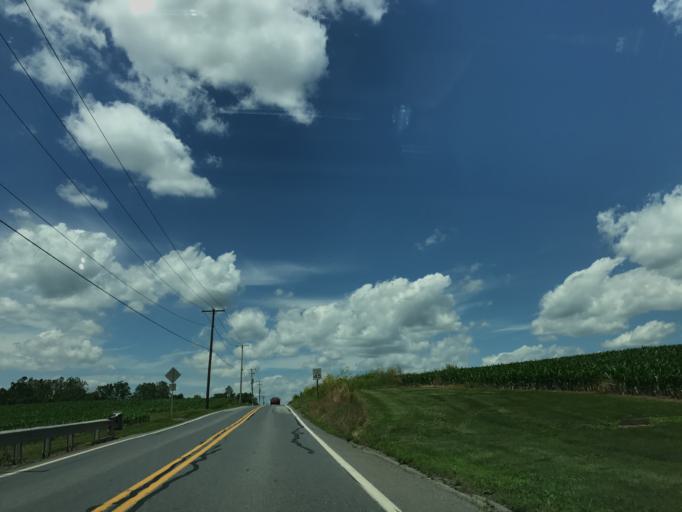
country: US
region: Pennsylvania
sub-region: Lancaster County
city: Mountville
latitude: 39.9679
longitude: -76.4547
